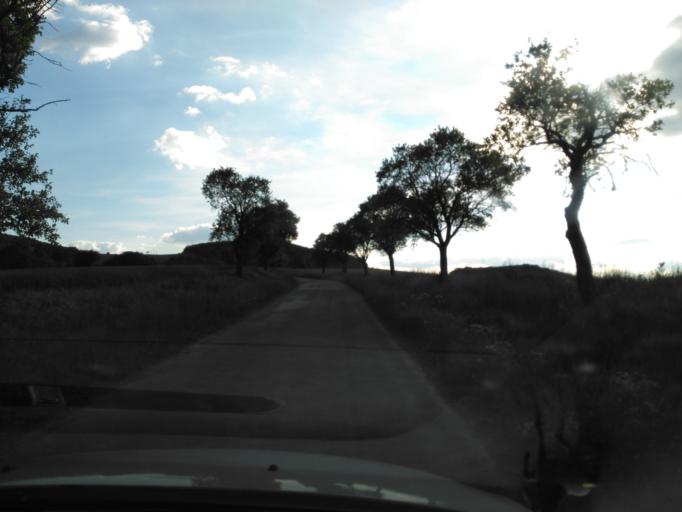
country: CZ
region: Central Bohemia
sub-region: Okres Beroun
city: Beroun
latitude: 49.9029
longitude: 14.1199
